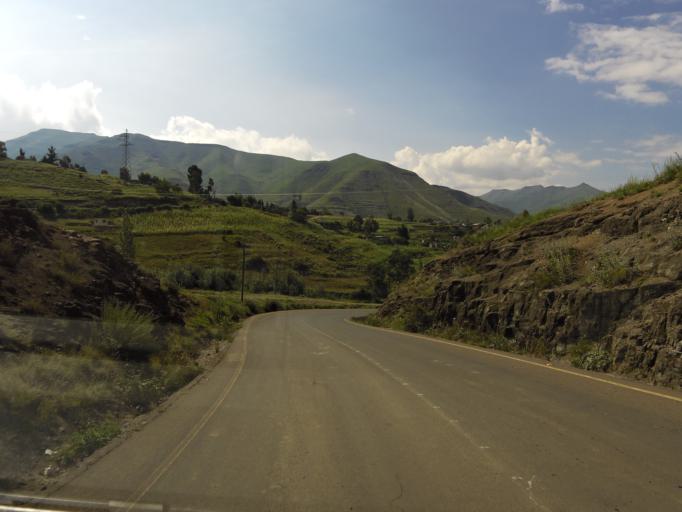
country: LS
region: Butha-Buthe
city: Butha-Buthe
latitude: -29.1148
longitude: 28.4908
